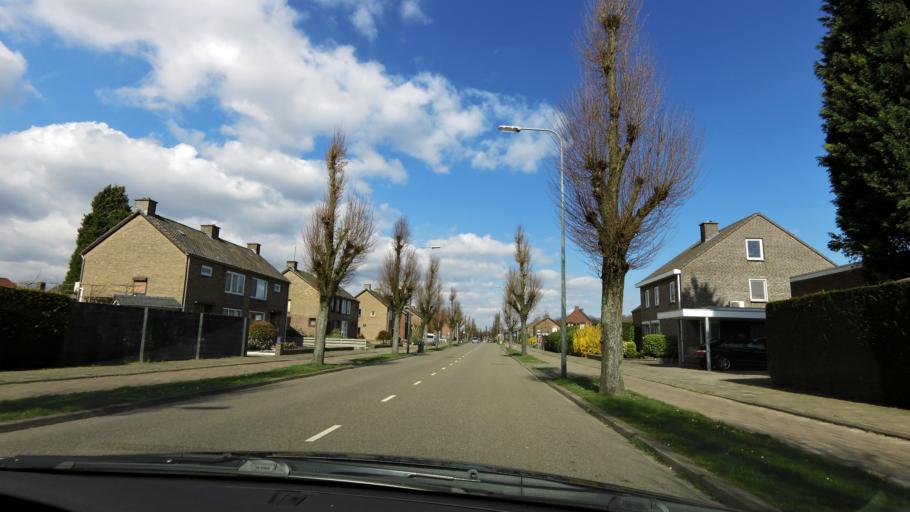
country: NL
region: Limburg
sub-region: Gemeente Stein
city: Stein
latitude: 50.9731
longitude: 5.7668
